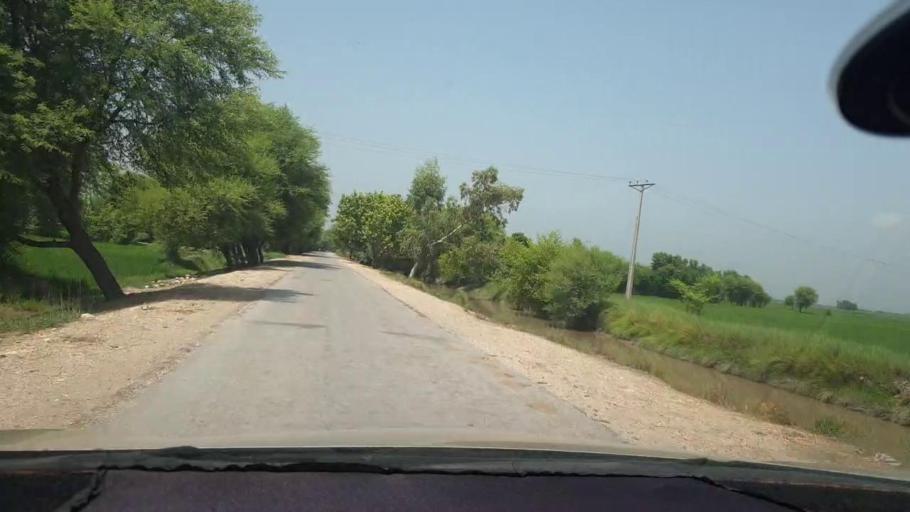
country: PK
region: Sindh
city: Kambar
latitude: 27.6531
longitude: 67.9638
